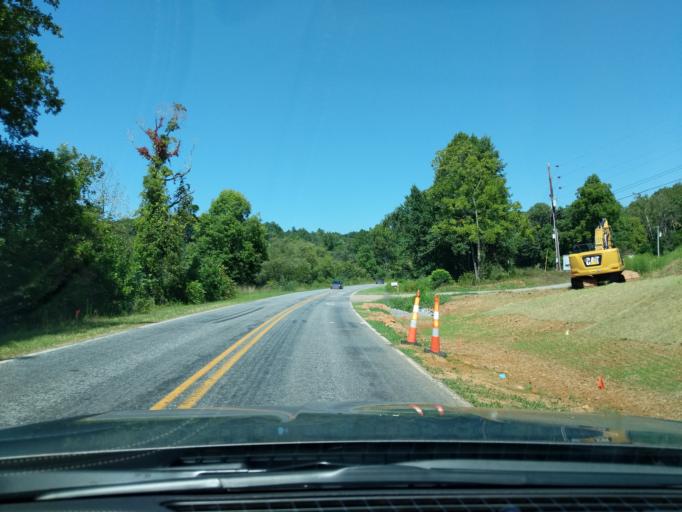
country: US
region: Georgia
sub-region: Towns County
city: Hiawassee
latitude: 35.0259
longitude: -83.7341
